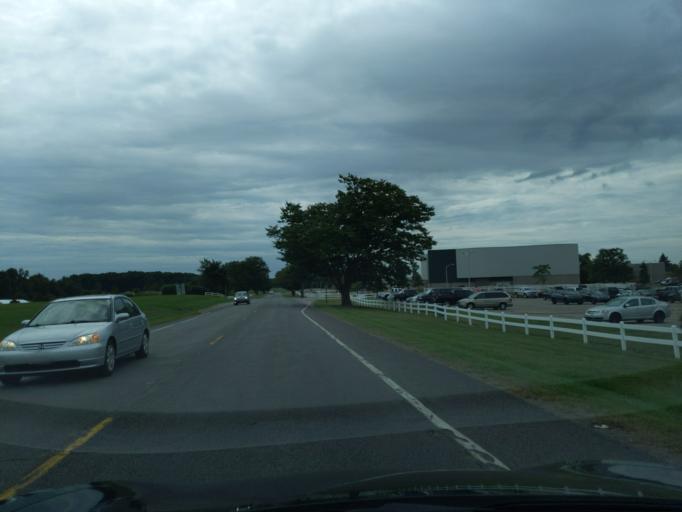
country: US
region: Michigan
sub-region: Ingham County
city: East Lansing
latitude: 42.7098
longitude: -84.4783
